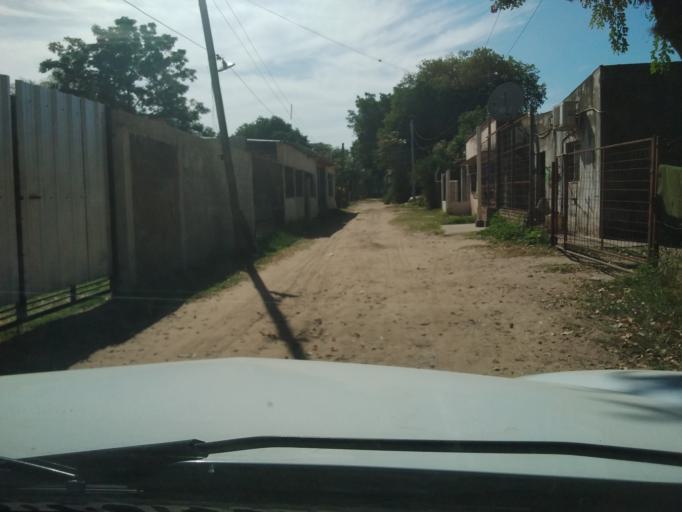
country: AR
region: Corrientes
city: Corrientes
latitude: -27.5103
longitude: -58.8081
